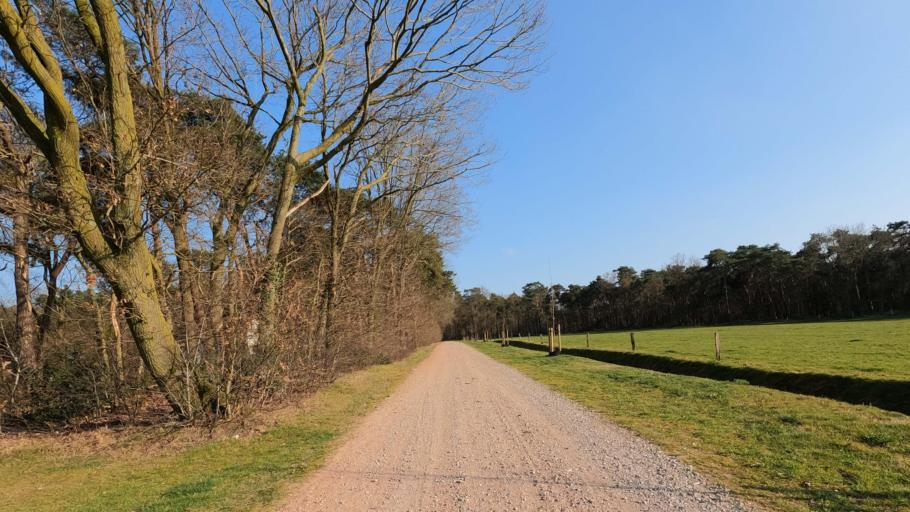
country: BE
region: Flanders
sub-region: Provincie Antwerpen
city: Baarle-Hertog
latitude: 51.3894
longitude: 4.8685
